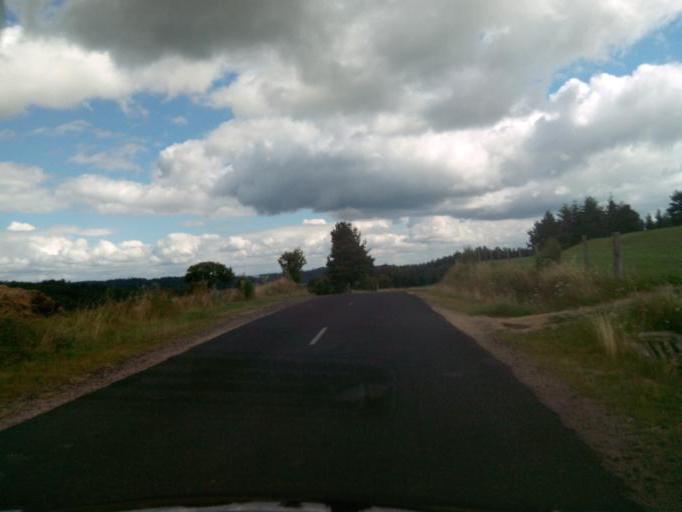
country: FR
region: Rhone-Alpes
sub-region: Departement de la Loire
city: Usson-en-Forez
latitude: 45.3637
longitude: 3.9923
